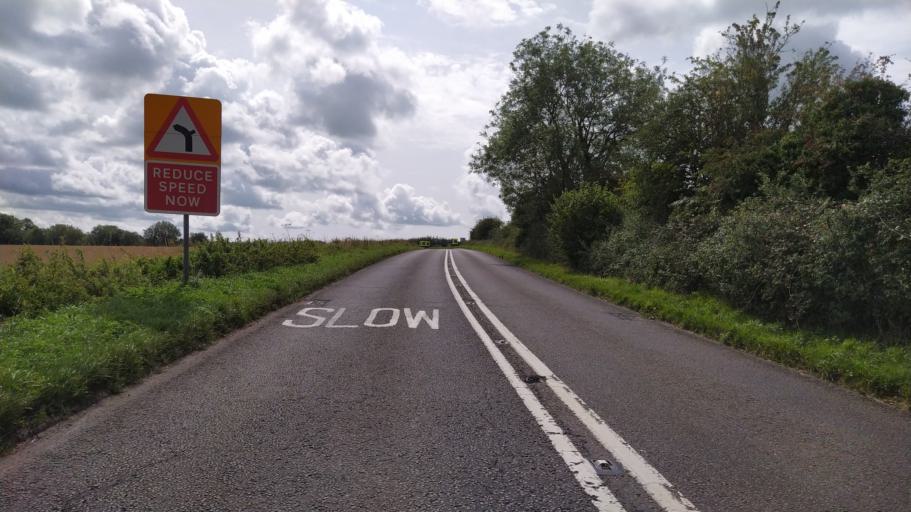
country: GB
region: England
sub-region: Wiltshire
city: Hindon
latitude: 51.0894
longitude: -2.1661
